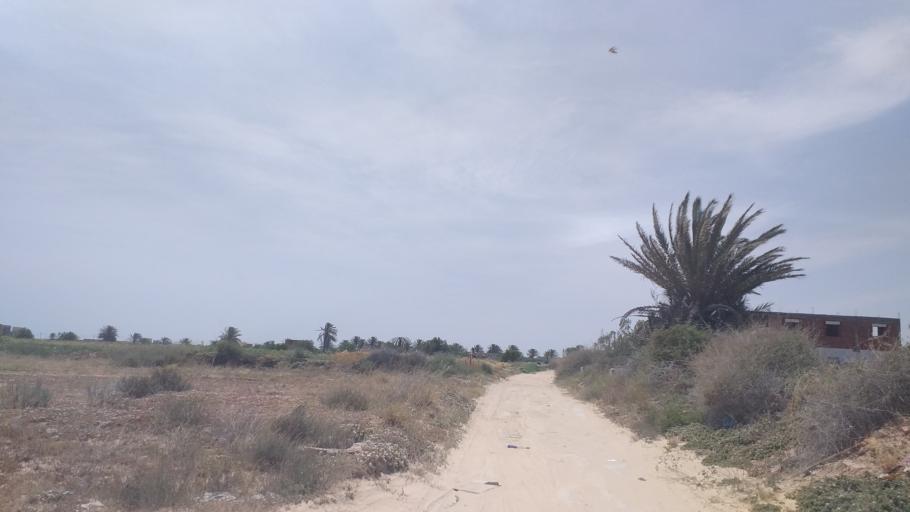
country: TN
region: Qabis
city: Gabes
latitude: 33.9550
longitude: 10.0630
